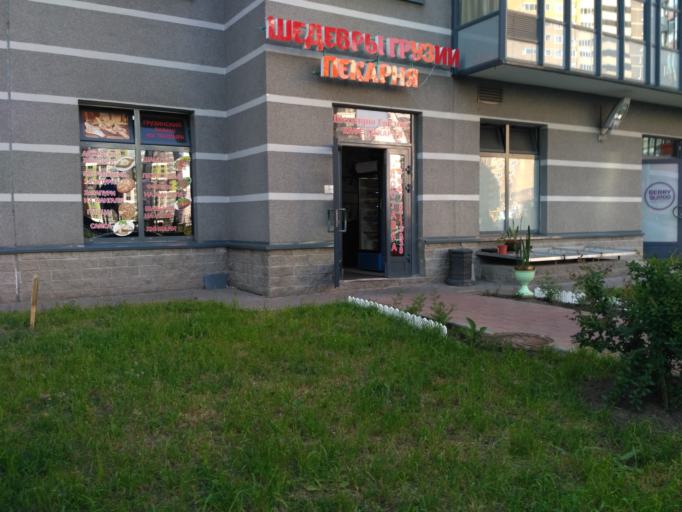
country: RU
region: St.-Petersburg
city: Kushelevka
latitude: 59.9879
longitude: 30.3701
